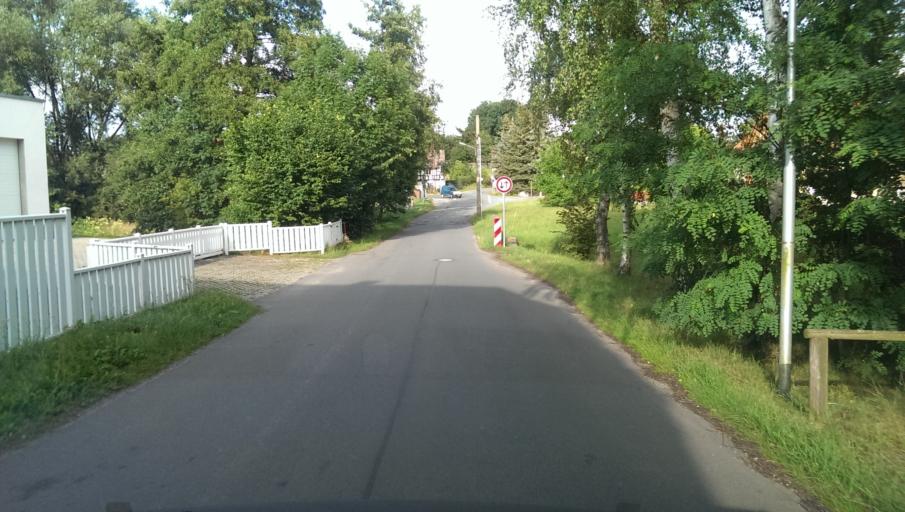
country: DE
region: Thuringia
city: Brahmenau
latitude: 50.9373
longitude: 12.1468
